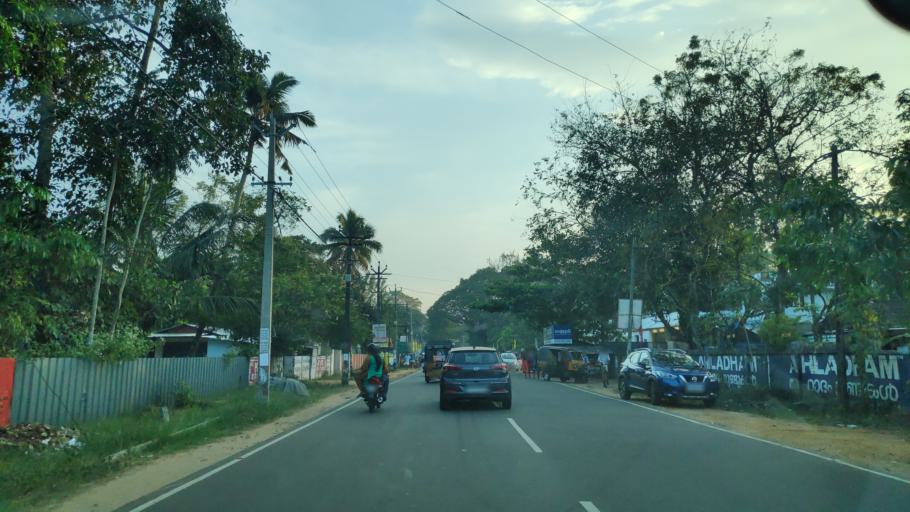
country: IN
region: Kerala
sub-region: Alappuzha
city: Shertallai
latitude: 9.6765
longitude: 76.3407
